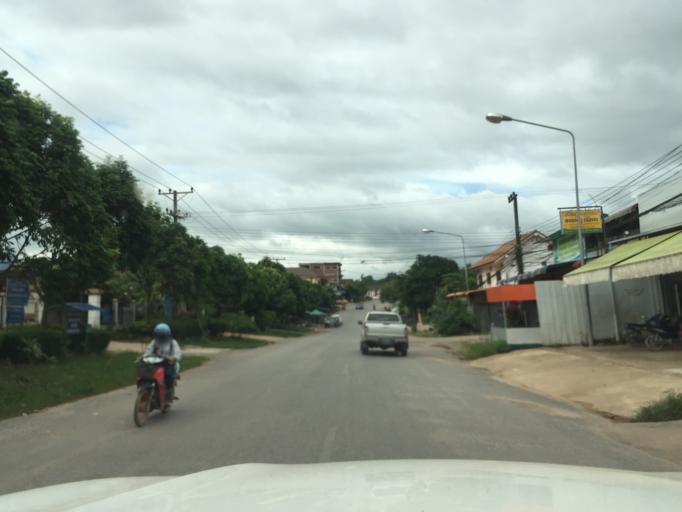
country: LA
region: Oudomxai
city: Muang Xay
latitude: 20.6962
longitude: 101.9889
